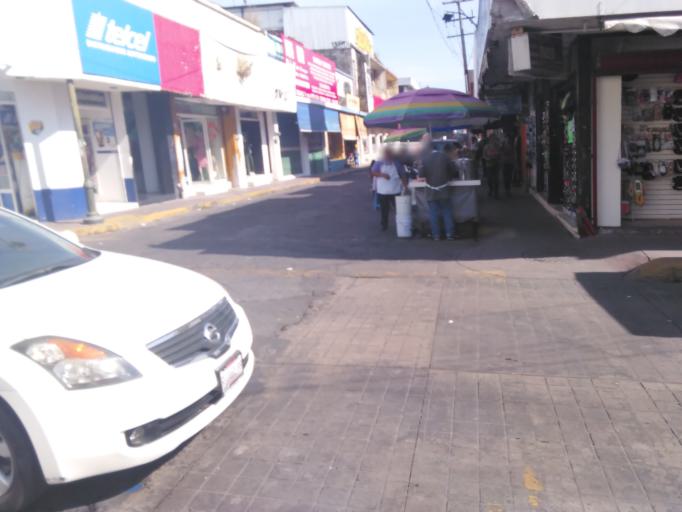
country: MX
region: Nayarit
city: Tepic
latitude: 21.5118
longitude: -104.8944
